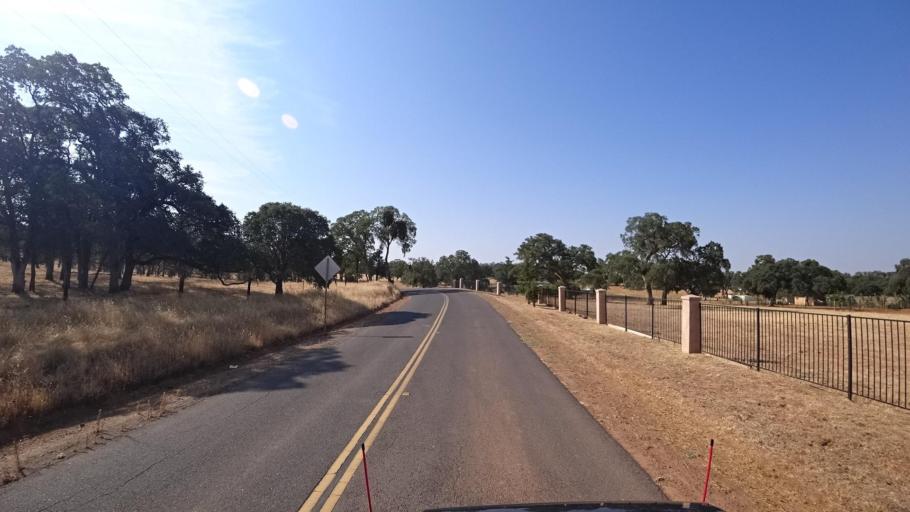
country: US
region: California
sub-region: Tuolumne County
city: Tuolumne City
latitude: 37.7046
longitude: -120.2954
